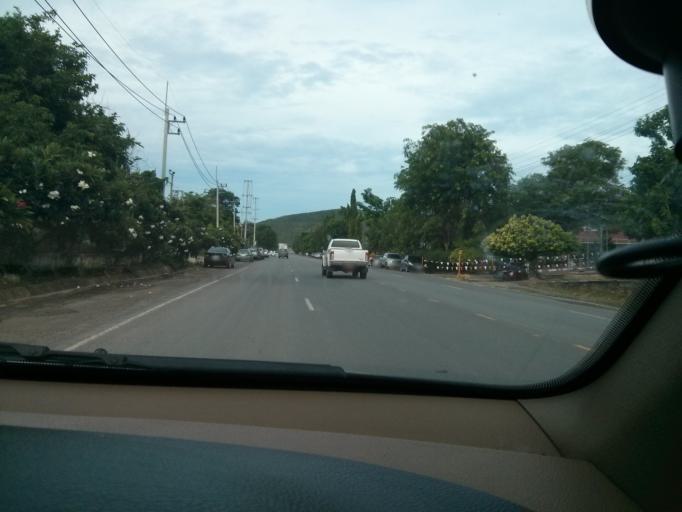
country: TH
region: Chon Buri
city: Sattahip
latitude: 12.6241
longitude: 100.9212
